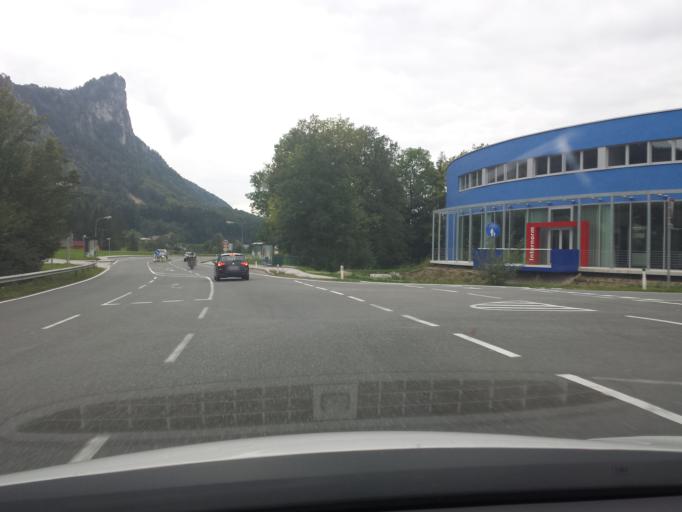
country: AT
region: Salzburg
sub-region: Politischer Bezirk Salzburg-Umgebung
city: Koppl
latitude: 47.8237
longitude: 13.1365
